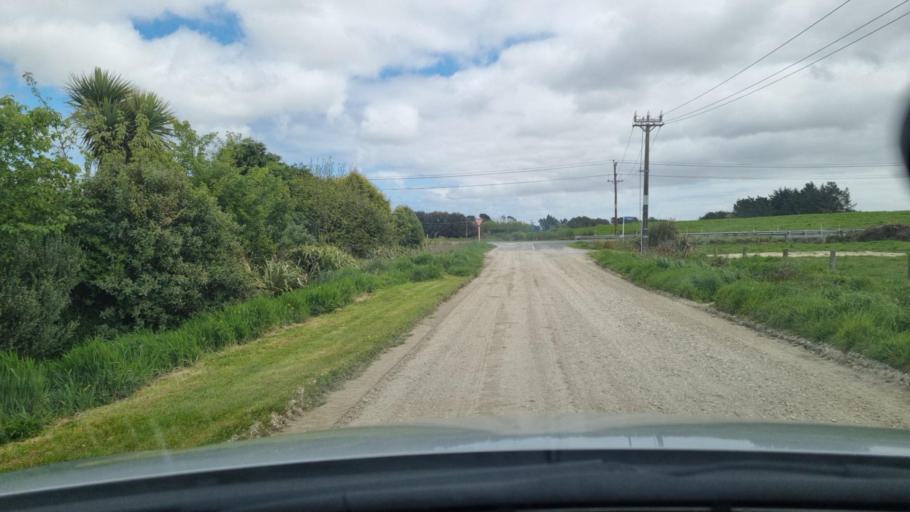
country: NZ
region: Southland
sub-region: Invercargill City
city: Invercargill
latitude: -46.4433
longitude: 168.4005
